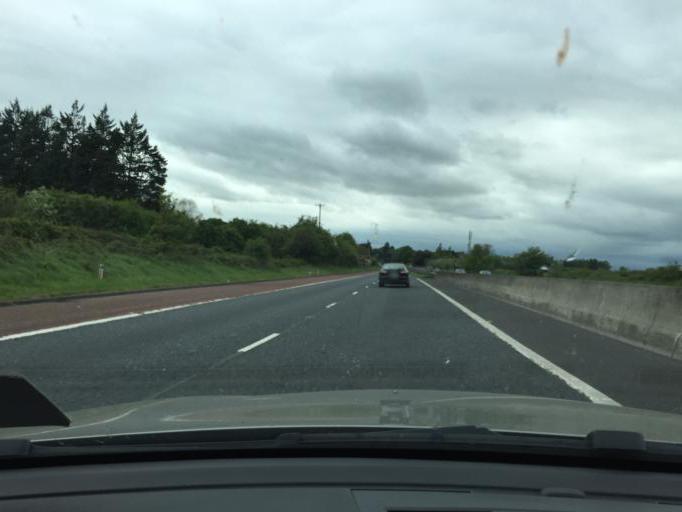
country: GB
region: Northern Ireland
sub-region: Lisburn District
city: Lisburn
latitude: 54.5121
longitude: -6.0165
